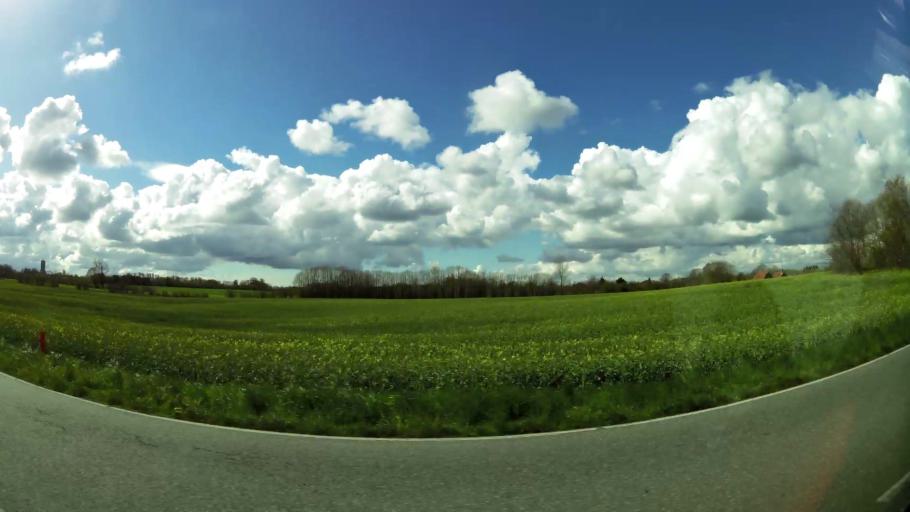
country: DK
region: South Denmark
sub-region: Middelfart Kommune
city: Brenderup
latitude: 55.4689
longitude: 10.0057
